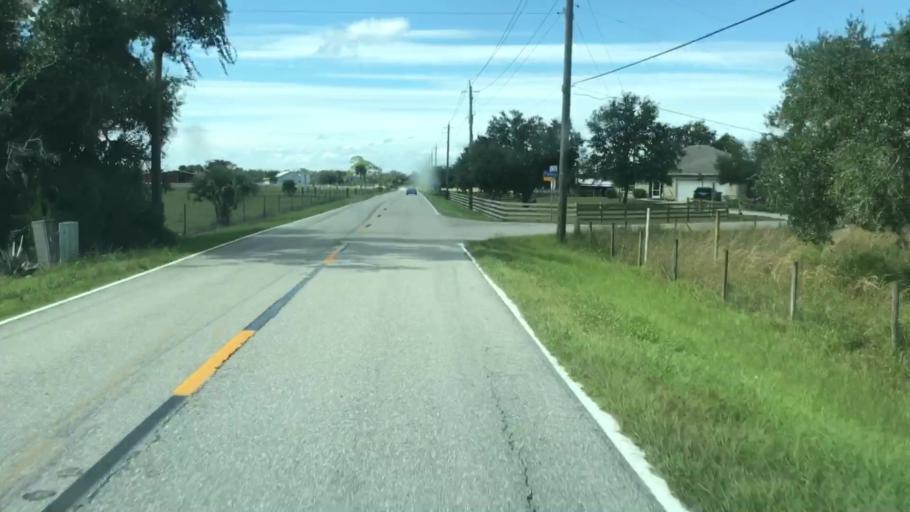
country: US
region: Florida
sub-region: Lee County
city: Alva
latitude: 26.7212
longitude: -81.6153
